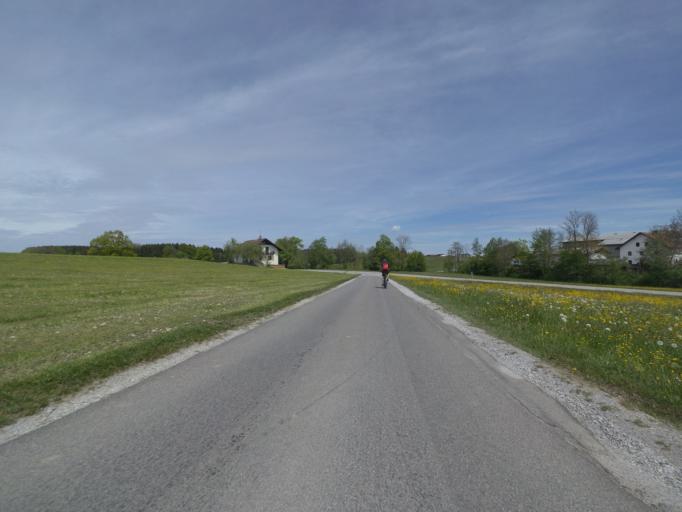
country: AT
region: Salzburg
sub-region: Politischer Bezirk Salzburg-Umgebung
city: Berndorf bei Salzburg
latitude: 47.9989
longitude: 13.0919
